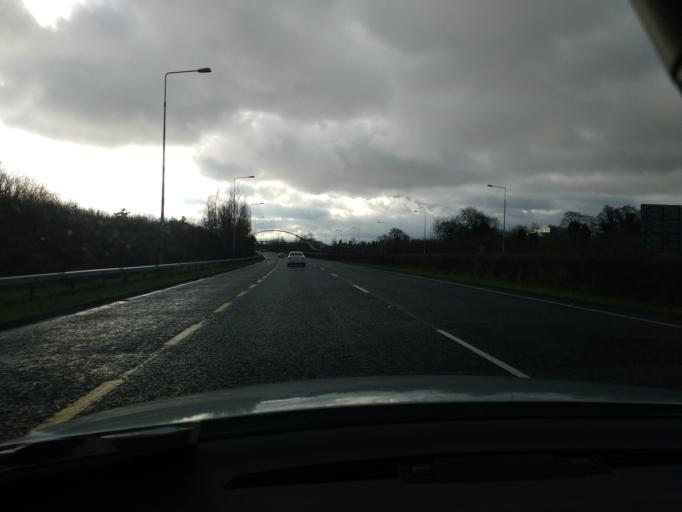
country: IE
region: Munster
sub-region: An Clar
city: Shannon
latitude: 52.7123
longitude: -8.8860
